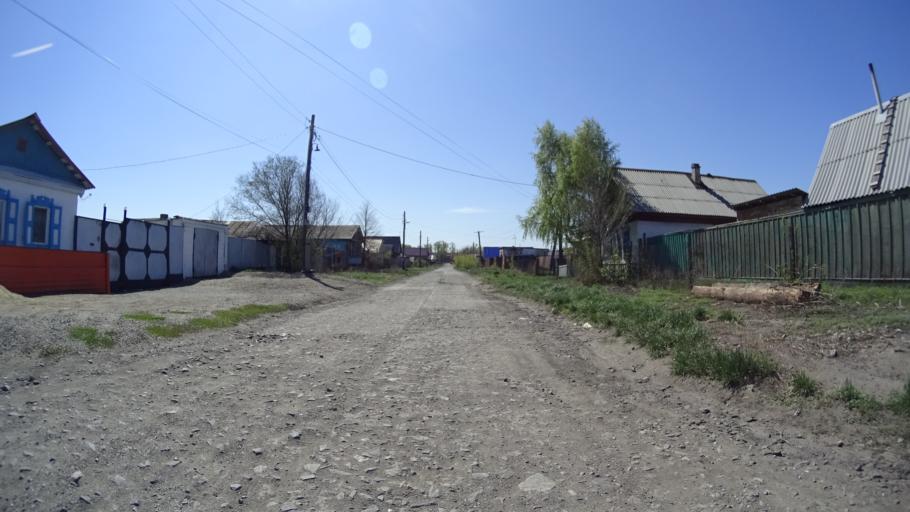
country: RU
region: Chelyabinsk
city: Troitsk
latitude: 54.0951
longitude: 61.5884
